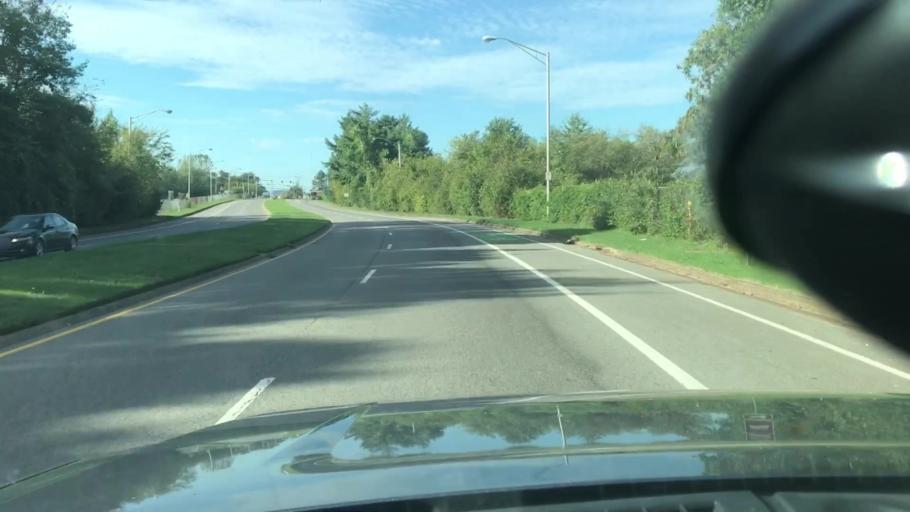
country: US
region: Tennessee
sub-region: Davidson County
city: Nashville
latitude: 36.1913
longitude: -86.8188
